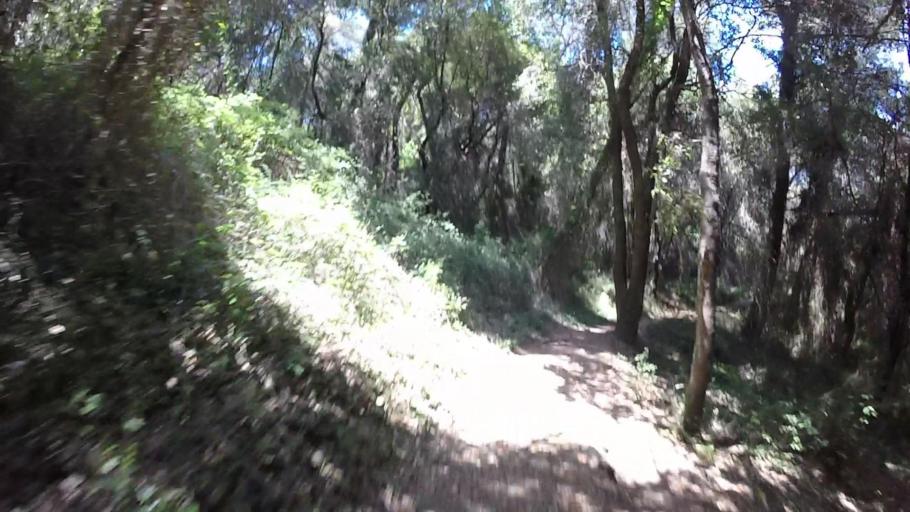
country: FR
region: Provence-Alpes-Cote d'Azur
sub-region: Departement des Alpes-Maritimes
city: Mougins
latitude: 43.5986
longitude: 7.0243
